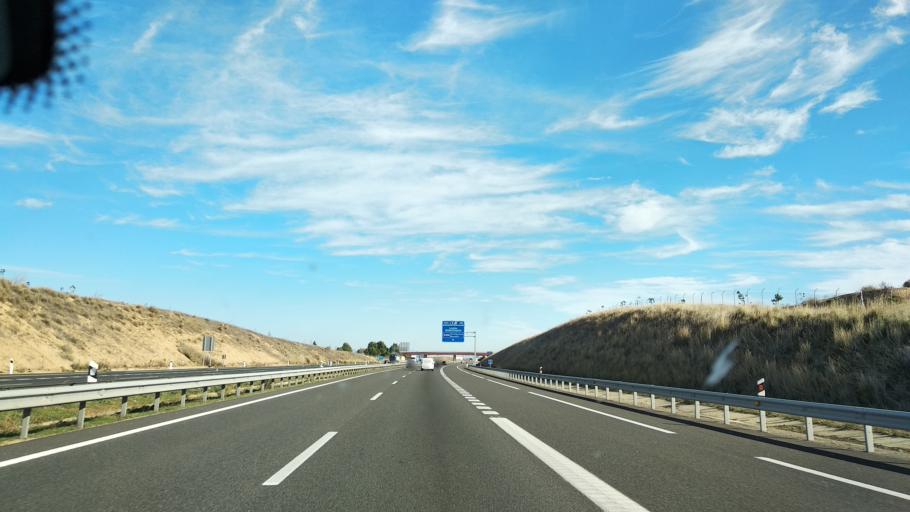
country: ES
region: Catalonia
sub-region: Provincia de Lleida
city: Torrefarrera
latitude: 41.6601
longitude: 0.5902
